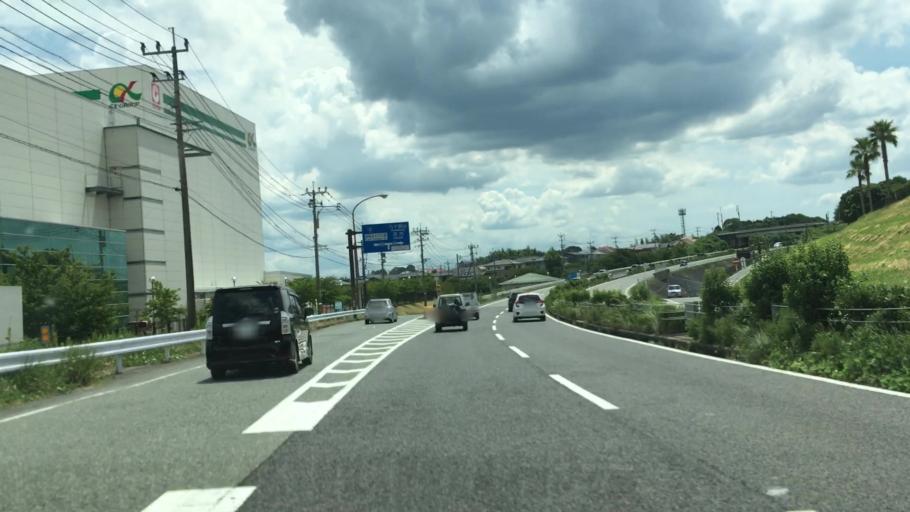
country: JP
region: Saga Prefecture
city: Tosu
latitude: 33.4050
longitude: 130.5135
